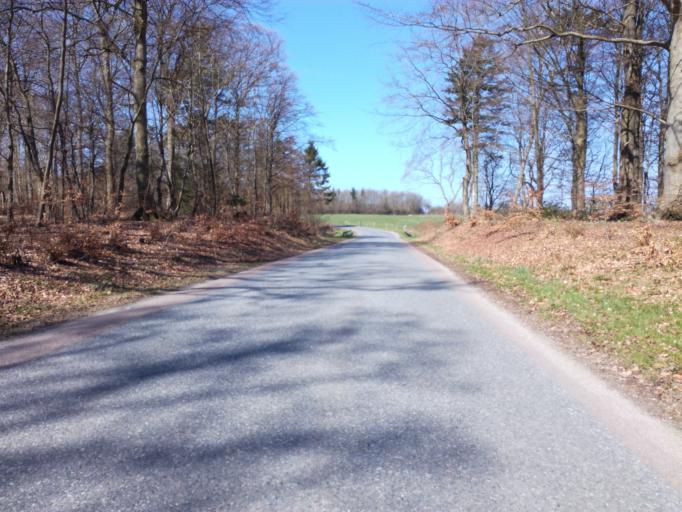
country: DK
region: South Denmark
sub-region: Fredericia Kommune
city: Fredericia
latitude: 55.6233
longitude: 9.8418
